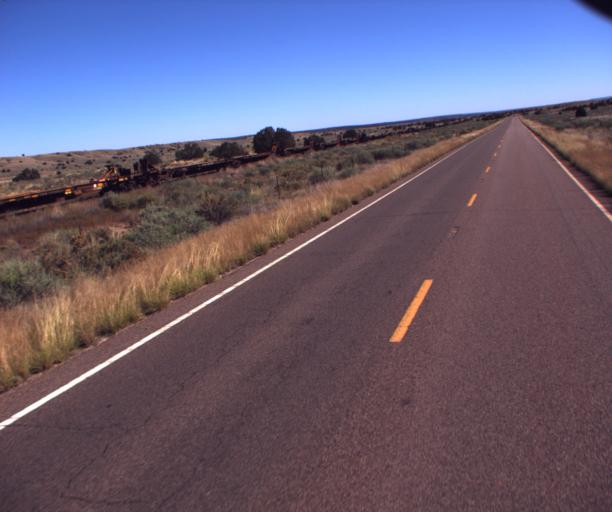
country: US
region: Arizona
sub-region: Navajo County
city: Snowflake
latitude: 34.5111
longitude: -110.1618
